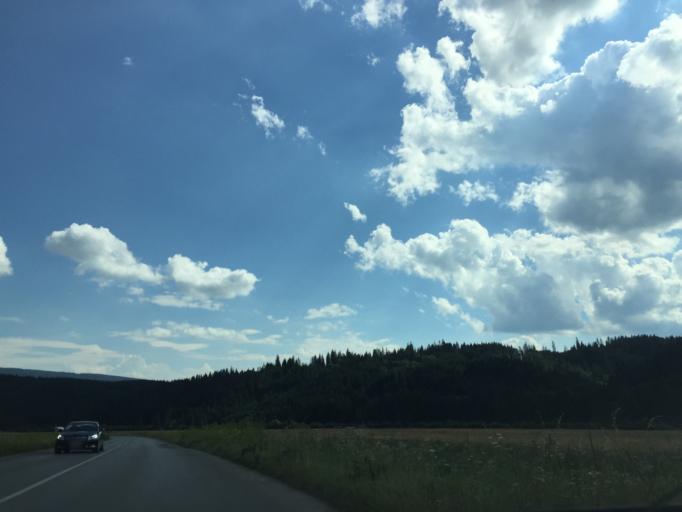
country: SK
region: Zilinsky
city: Namestovo
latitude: 49.3785
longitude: 19.3871
